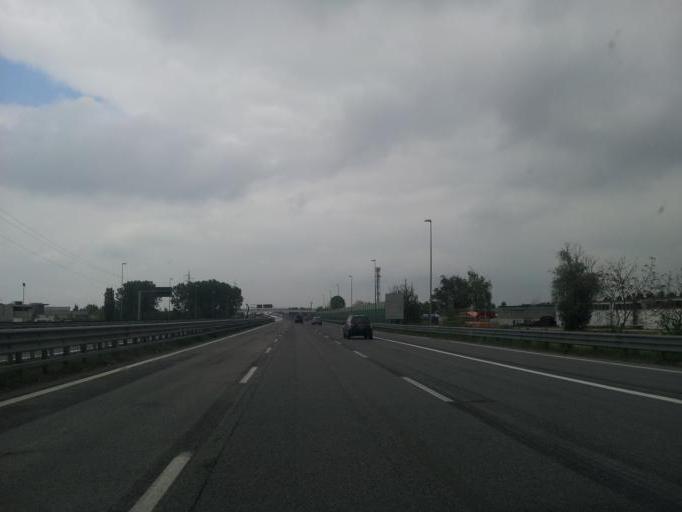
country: IT
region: Veneto
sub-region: Provincia di Venezia
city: Quarto d'Altino
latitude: 45.5763
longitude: 12.3493
